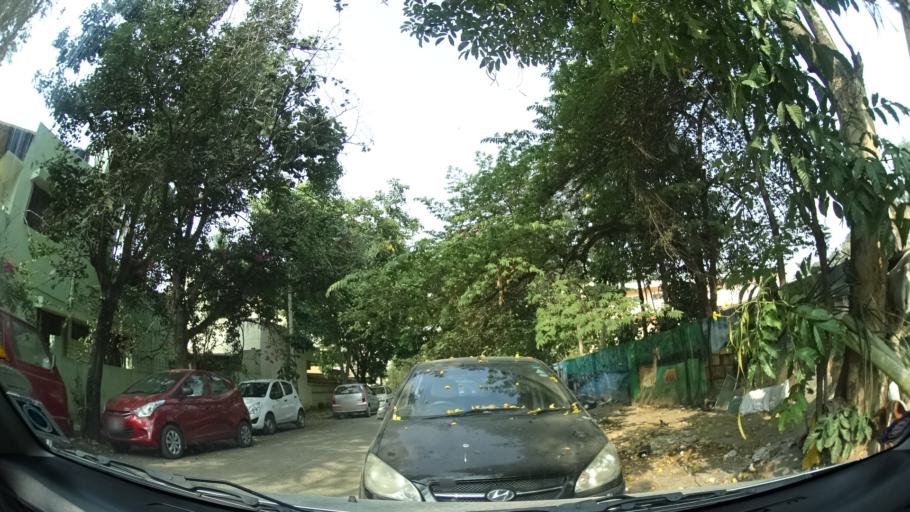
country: IN
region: Karnataka
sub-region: Bangalore Urban
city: Yelahanka
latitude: 13.0420
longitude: 77.5717
